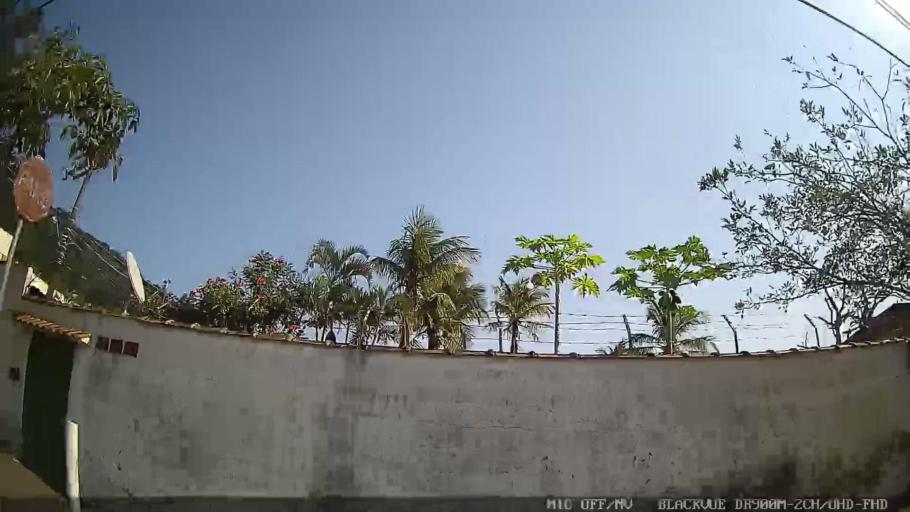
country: BR
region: Sao Paulo
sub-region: Guaruja
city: Guaruja
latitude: -23.9909
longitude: -46.2633
